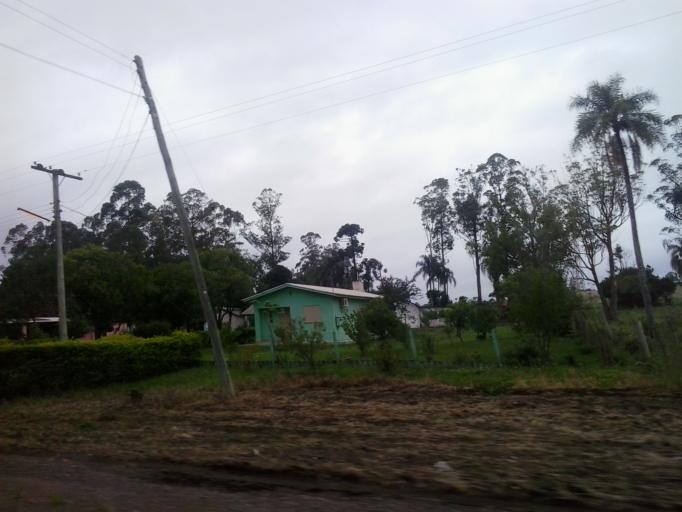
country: BR
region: Rio Grande do Sul
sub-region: Santa Maria
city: Santa Maria
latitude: -29.7224
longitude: -53.3715
